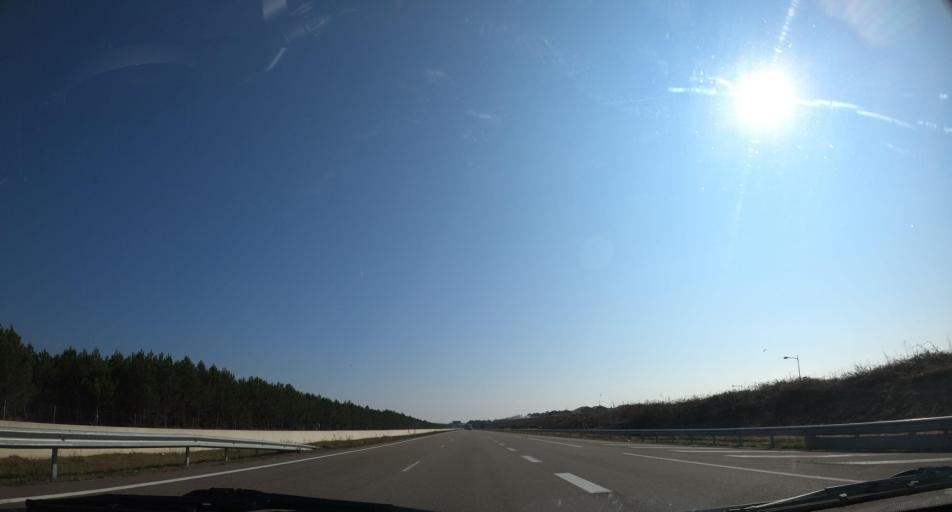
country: FR
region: Aquitaine
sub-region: Departement des Landes
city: Saint-Geours-de-Maremne
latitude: 43.6963
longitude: -1.2233
